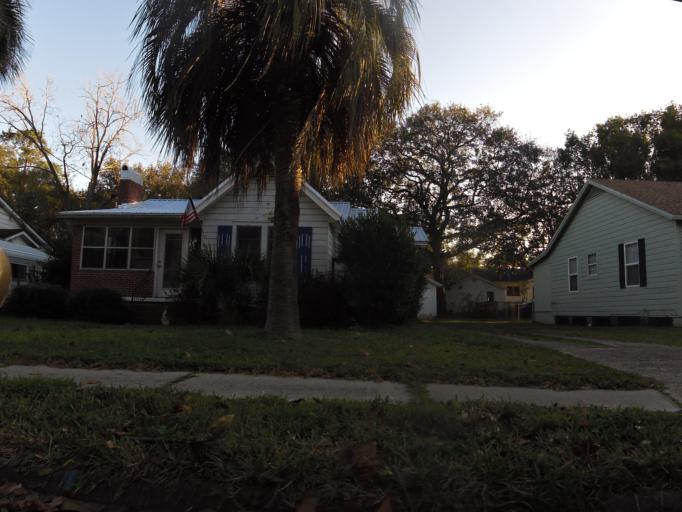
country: US
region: Florida
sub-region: Duval County
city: Jacksonville
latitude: 30.3176
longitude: -81.7072
